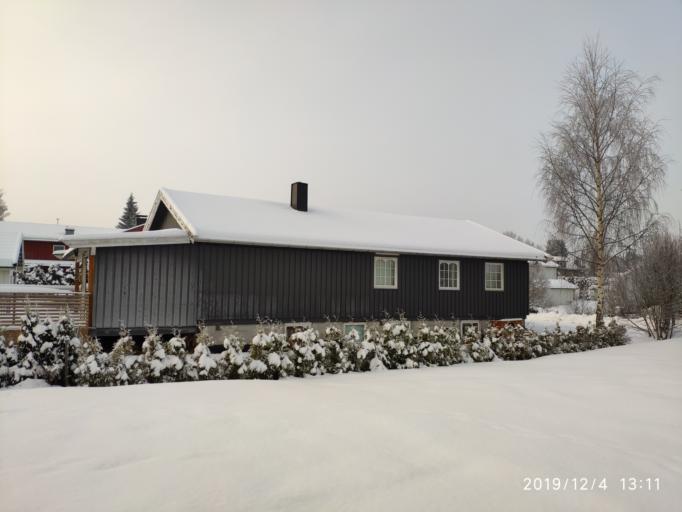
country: NO
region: Hedmark
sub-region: Elverum
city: Elverum
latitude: 60.8873
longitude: 11.5405
